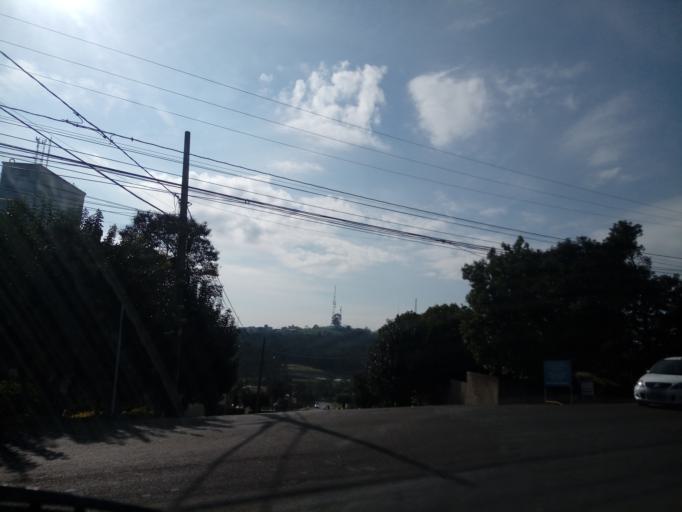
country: BR
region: Santa Catarina
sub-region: Chapeco
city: Chapeco
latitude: -27.1085
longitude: -52.5940
